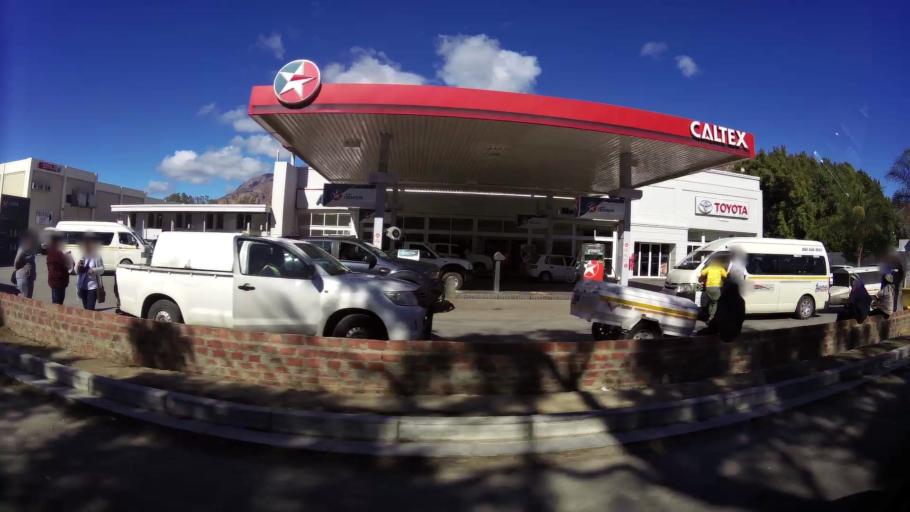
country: ZA
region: Western Cape
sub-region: Cape Winelands District Municipality
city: Ashton
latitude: -33.7888
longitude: 20.1232
